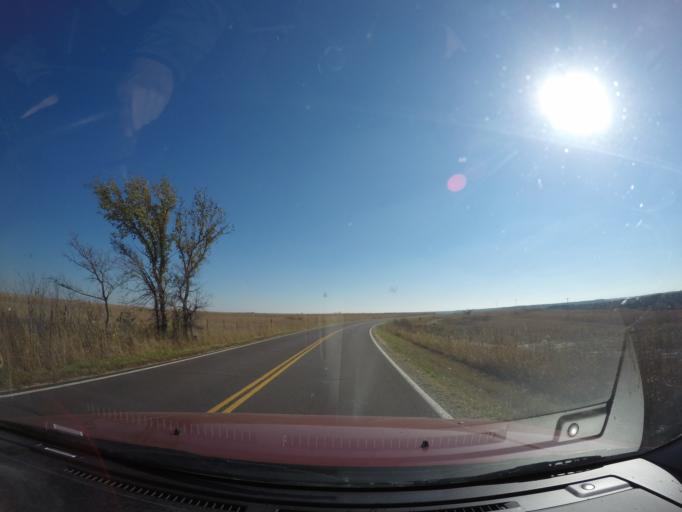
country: US
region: Kansas
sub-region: Geary County
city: Grandview Plaza
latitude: 39.0144
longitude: -96.7551
